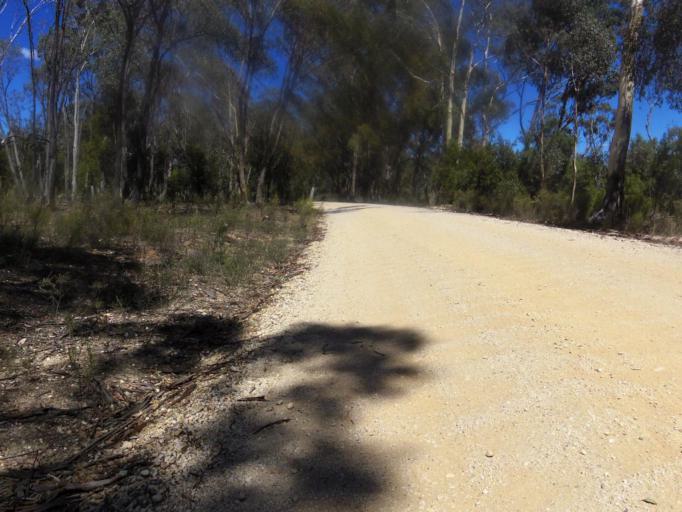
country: AU
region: Victoria
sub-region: Mount Alexander
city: Castlemaine
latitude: -37.0474
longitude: 144.1814
